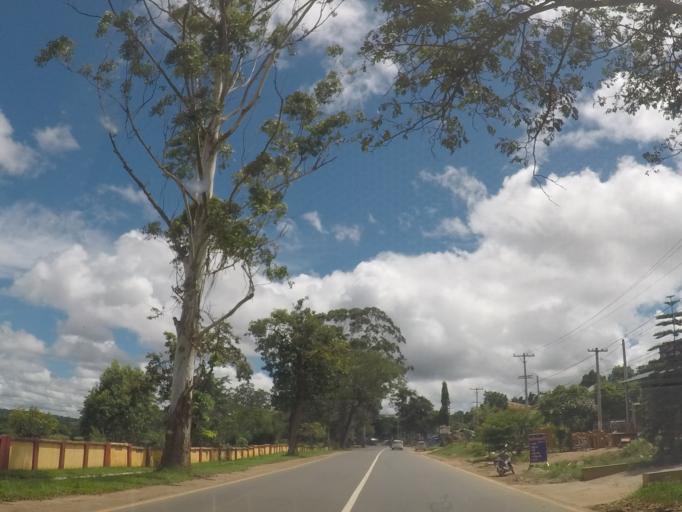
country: MM
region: Mandalay
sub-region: Pyin Oo Lwin District
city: Pyin Oo Lwin
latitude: 22.0432
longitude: 96.5046
